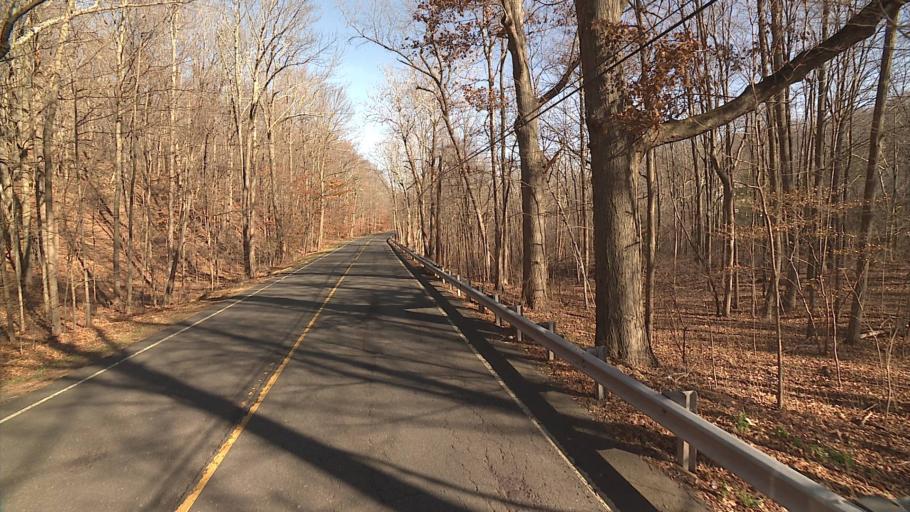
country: US
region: Connecticut
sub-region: Middlesex County
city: Durham
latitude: 41.4341
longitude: -72.7271
